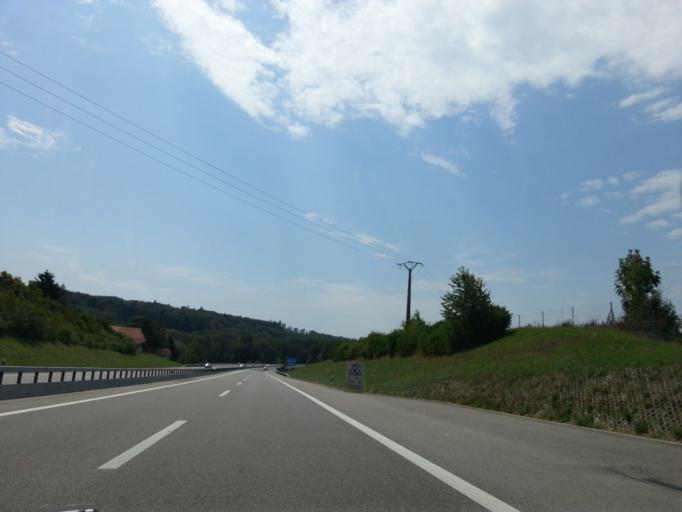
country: CH
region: Fribourg
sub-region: See District
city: Kerzers
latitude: 46.9526
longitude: 7.1664
